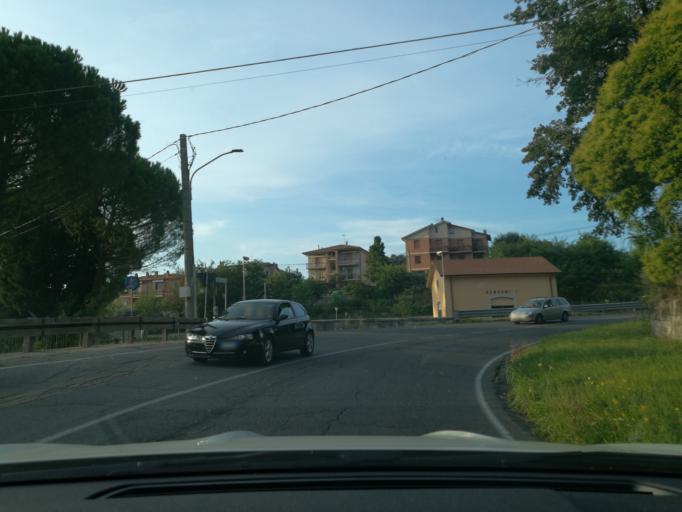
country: IT
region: Umbria
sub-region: Provincia di Terni
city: San Gemini
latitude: 42.6238
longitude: 12.5486
